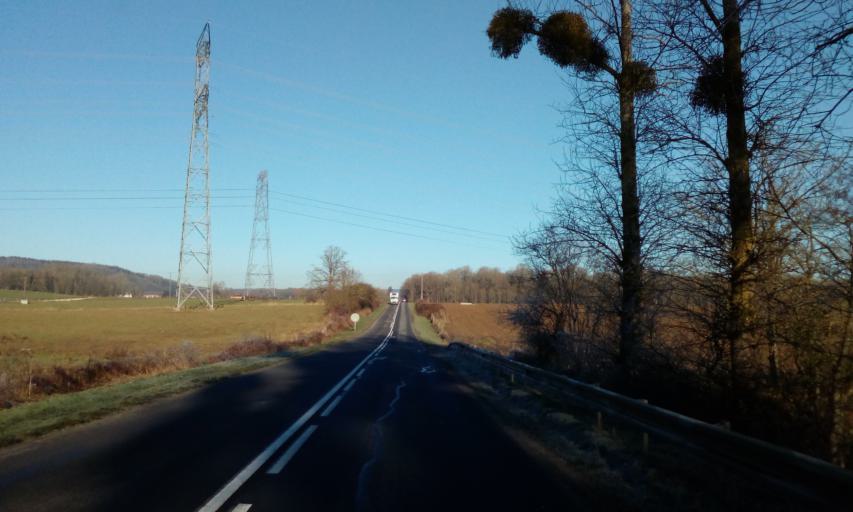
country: FR
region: Champagne-Ardenne
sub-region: Departement des Ardennes
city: Rimogne
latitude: 49.7994
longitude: 4.5115
